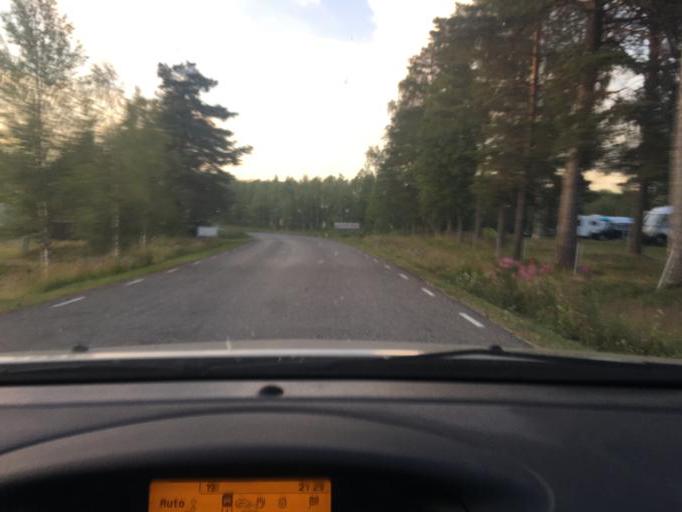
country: SE
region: Norrbotten
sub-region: Kalix Kommun
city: Toere
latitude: 65.9021
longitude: 22.6563
